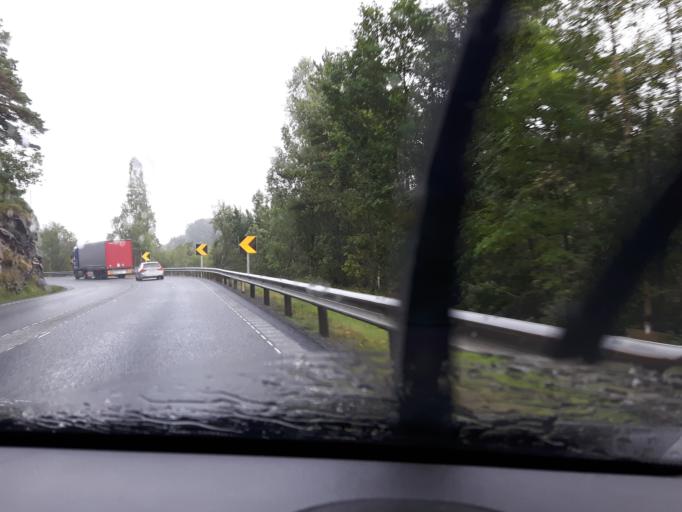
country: NO
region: Vest-Agder
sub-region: Sogne
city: Sogne
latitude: 58.0969
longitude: 7.6844
